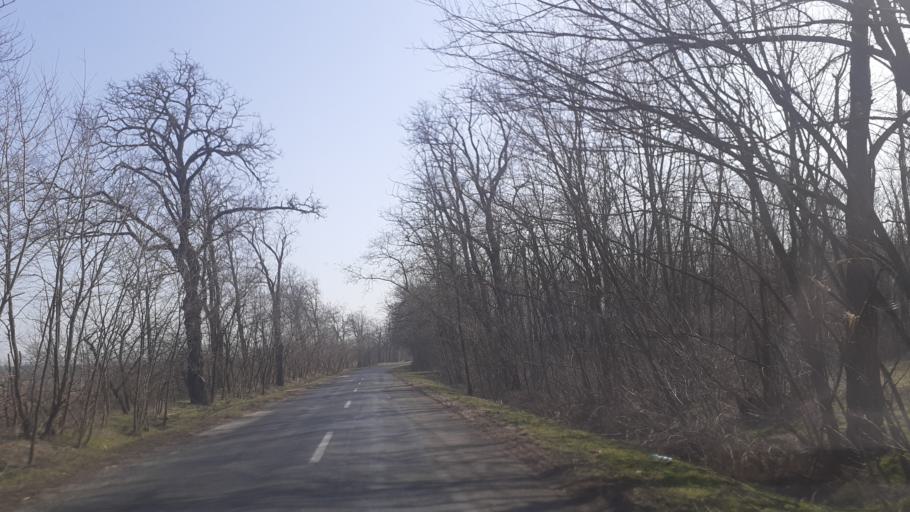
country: HU
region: Pest
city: Orkeny
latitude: 47.0733
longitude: 19.3802
